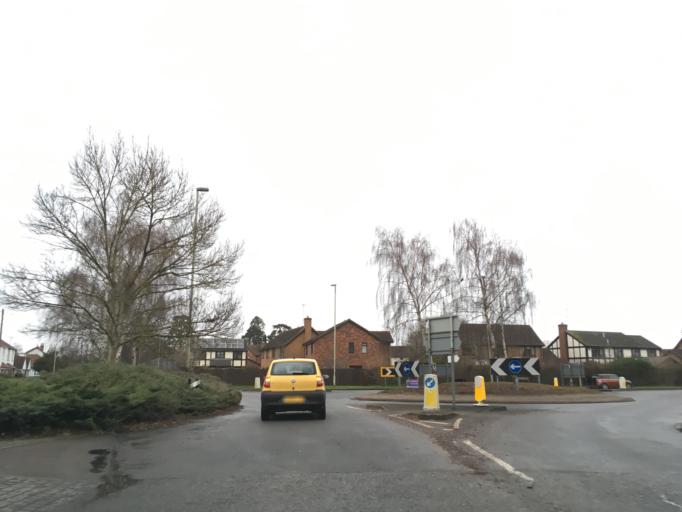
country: GB
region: England
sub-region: Gloucestershire
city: Shurdington
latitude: 51.8849
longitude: -2.1251
